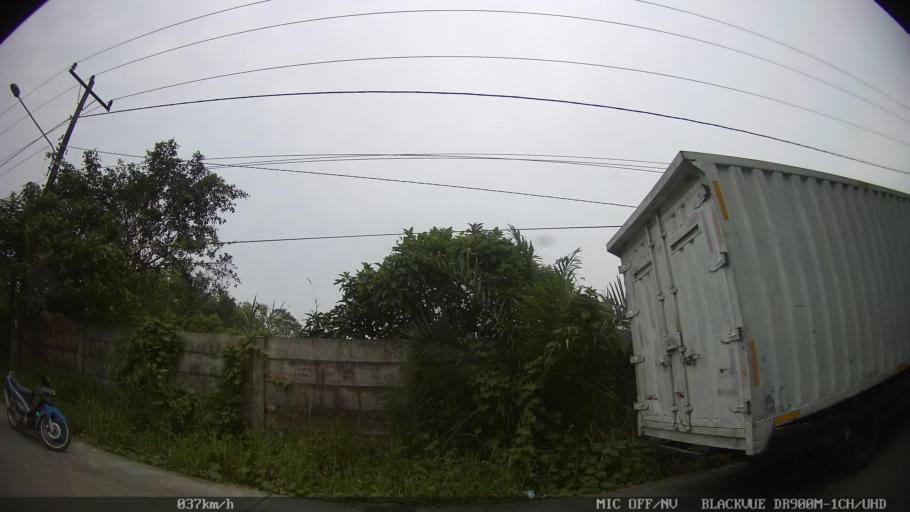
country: ID
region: North Sumatra
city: Deli Tua
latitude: 3.5339
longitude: 98.7260
